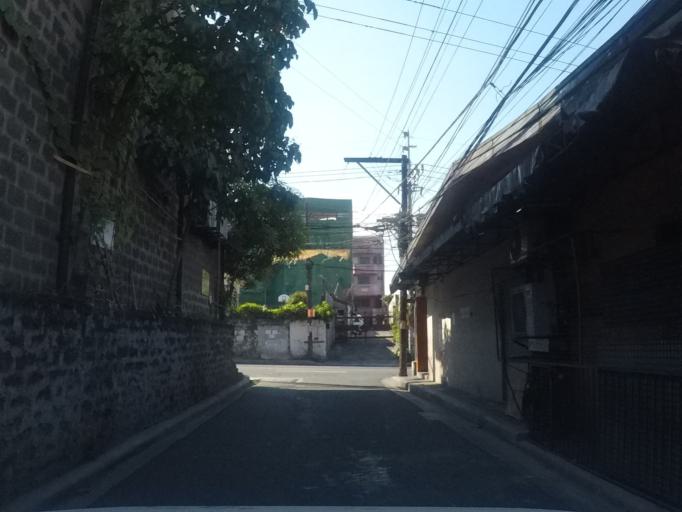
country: PH
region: Metro Manila
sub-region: San Juan
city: San Juan
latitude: 14.6083
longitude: 121.0288
